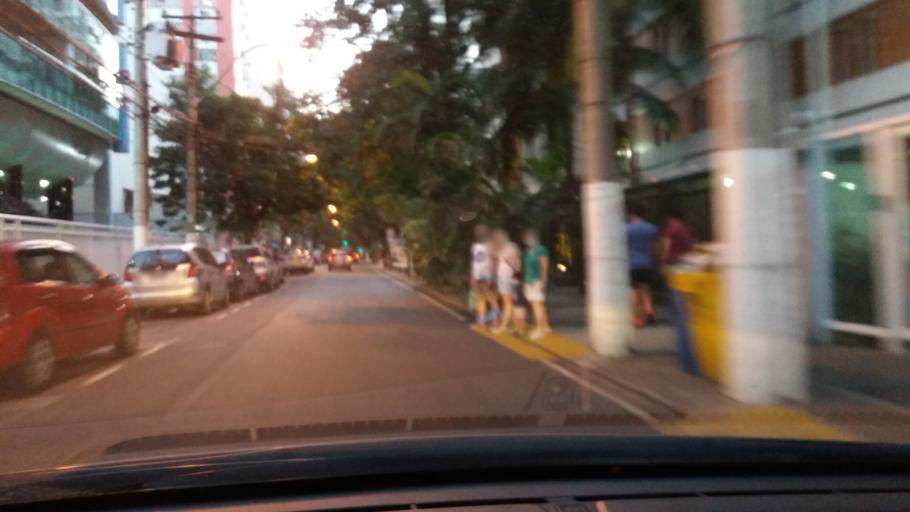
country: BR
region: Rio de Janeiro
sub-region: Niteroi
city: Niteroi
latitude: -22.9022
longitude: -43.1035
